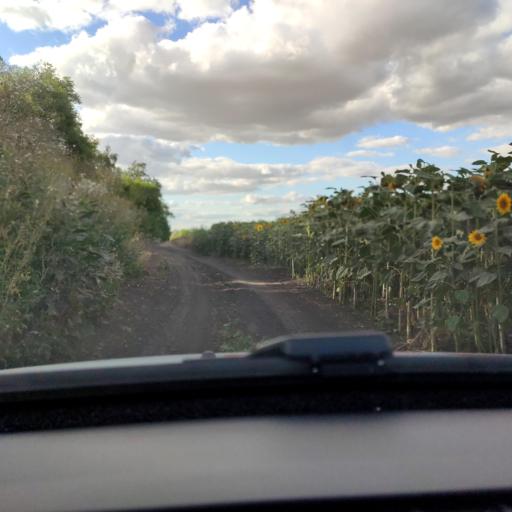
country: RU
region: Voronezj
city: Verkhnyaya Khava
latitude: 51.6029
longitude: 39.8389
